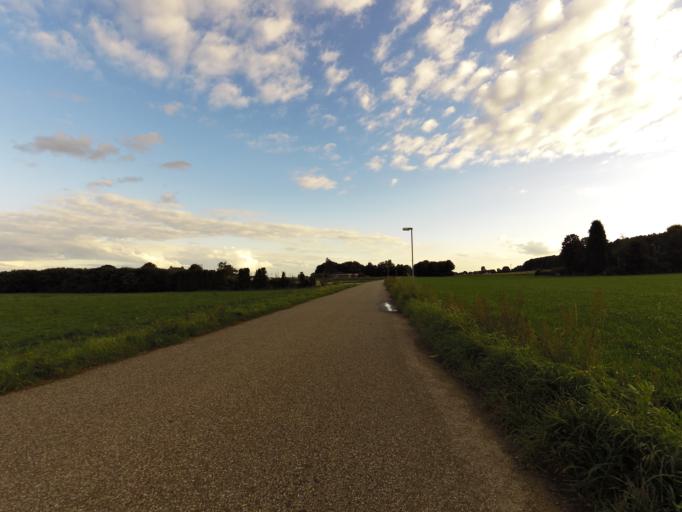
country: NL
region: Gelderland
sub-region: Gemeente Montferland
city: s-Heerenberg
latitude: 51.8933
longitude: 6.2643
